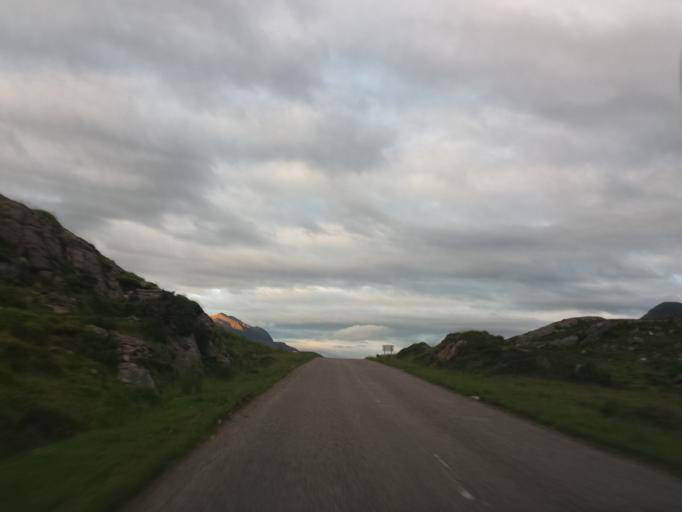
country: GB
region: Scotland
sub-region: Highland
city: Portree
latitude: 57.5258
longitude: -5.6421
